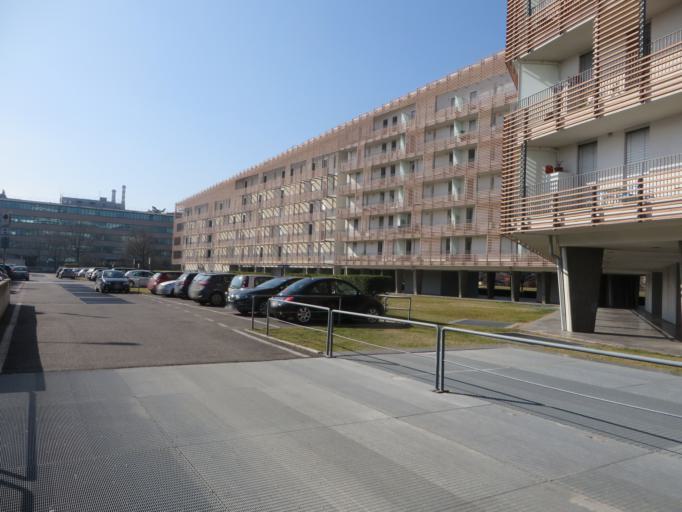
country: IT
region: Lombardy
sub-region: Provincia di Brescia
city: Brescia
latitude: 45.5214
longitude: 10.2163
